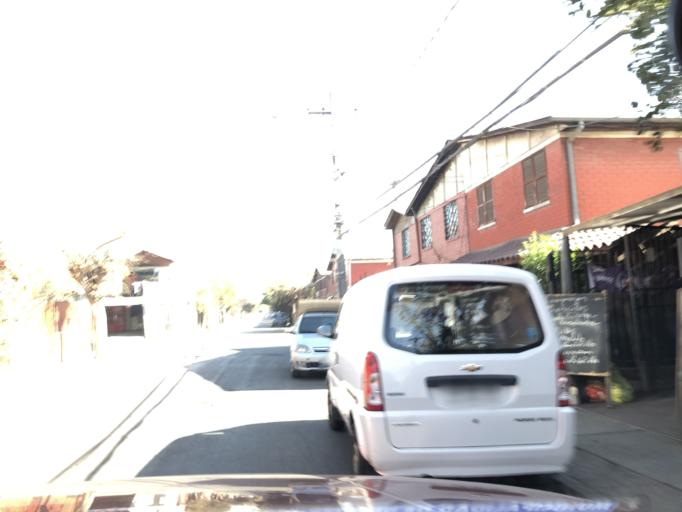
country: CL
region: Santiago Metropolitan
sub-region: Provincia de Cordillera
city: Puente Alto
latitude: -33.5643
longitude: -70.5769
